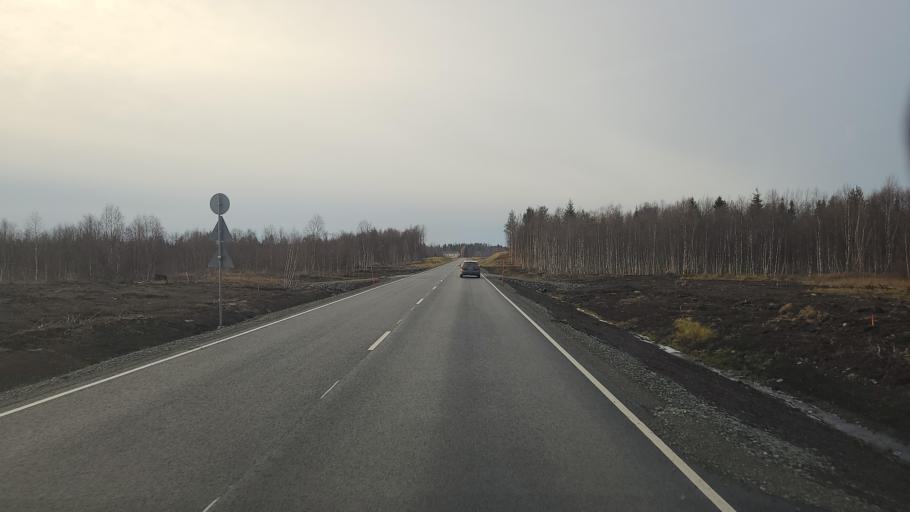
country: FI
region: Lapland
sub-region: Tunturi-Lappi
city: Kittilae
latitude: 67.8648
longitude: 24.9597
